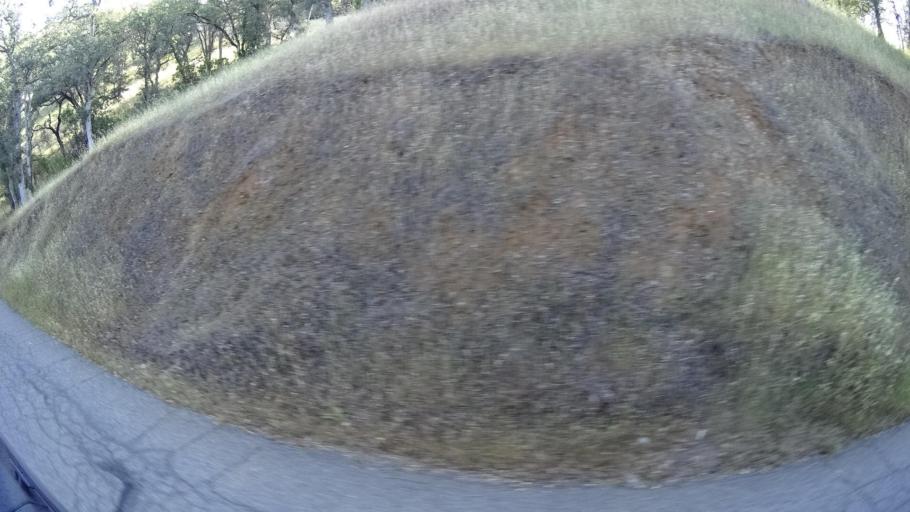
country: US
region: California
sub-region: Lake County
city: Nice
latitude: 39.1222
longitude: -122.8364
